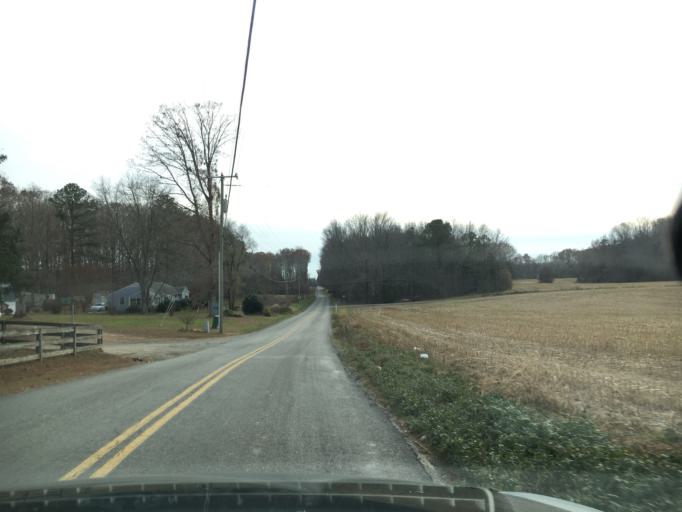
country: US
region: Virginia
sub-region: Henrico County
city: Wyndham
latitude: 37.6980
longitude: -77.6829
